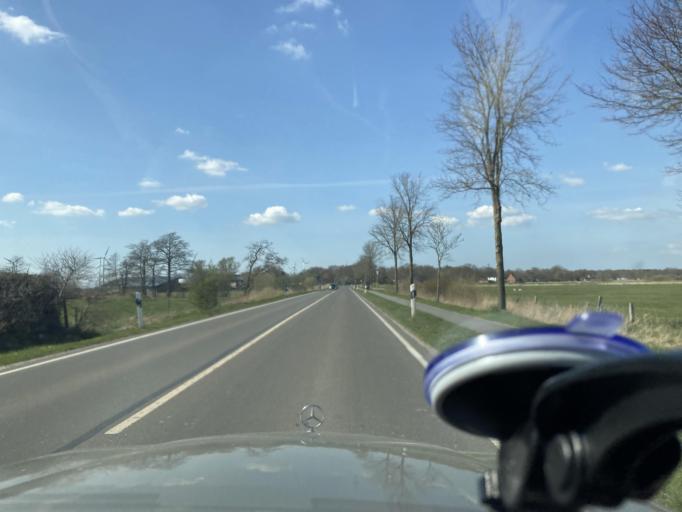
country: DE
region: Schleswig-Holstein
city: Stelle-Wittenwurth
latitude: 54.2596
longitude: 9.0568
